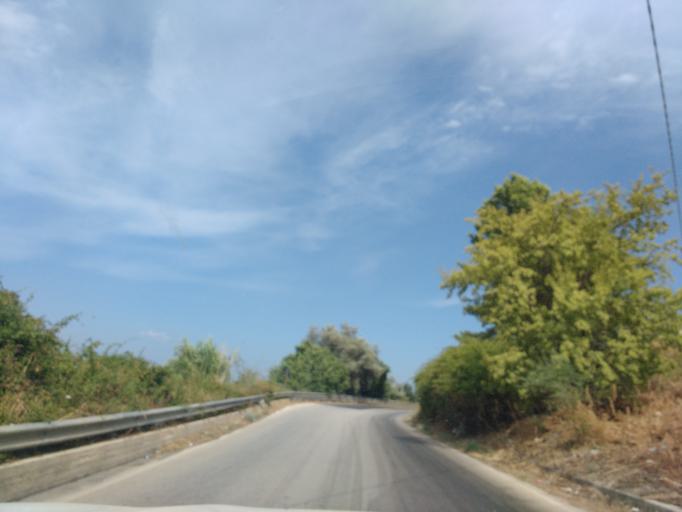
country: IT
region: Sicily
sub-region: Provincia di Siracusa
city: Noto
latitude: 36.8799
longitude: 15.0675
